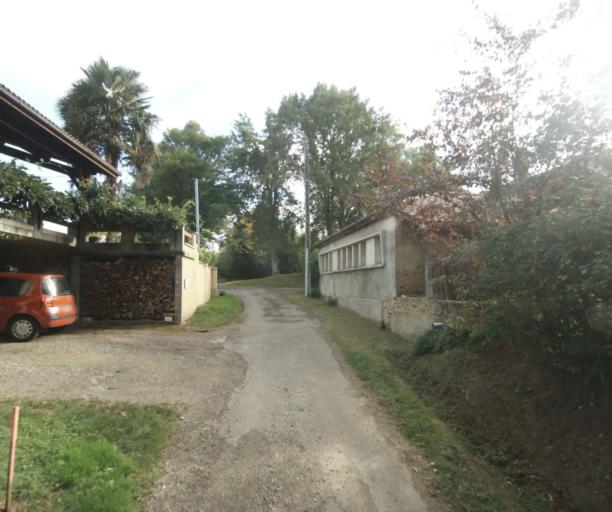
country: FR
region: Midi-Pyrenees
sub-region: Departement du Gers
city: Cazaubon
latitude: 43.8693
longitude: -0.1040
